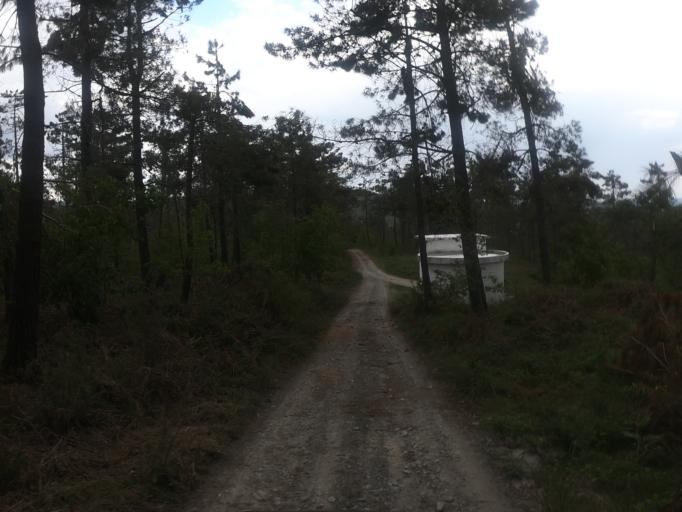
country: PT
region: Vila Real
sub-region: Mondim de Basto
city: Mondim de Basto
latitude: 41.3103
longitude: -7.8845
